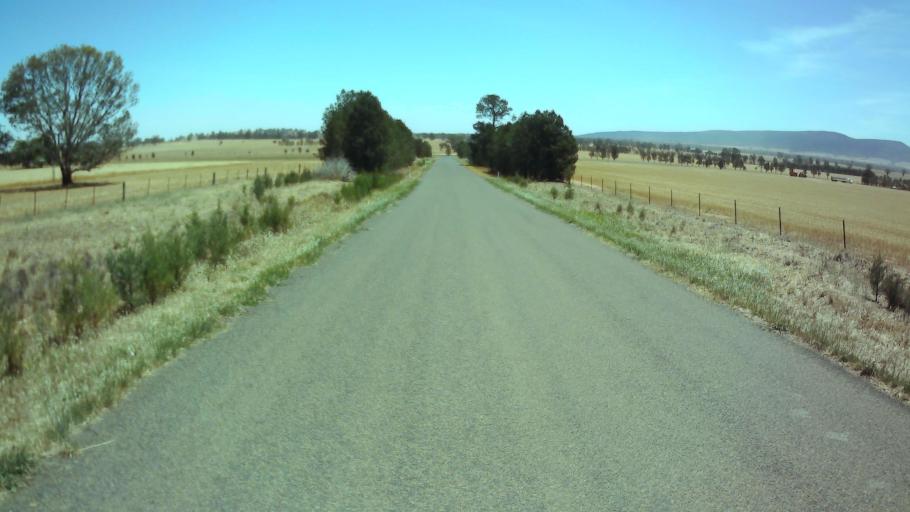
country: AU
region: New South Wales
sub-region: Weddin
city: Grenfell
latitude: -34.0497
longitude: 148.1787
